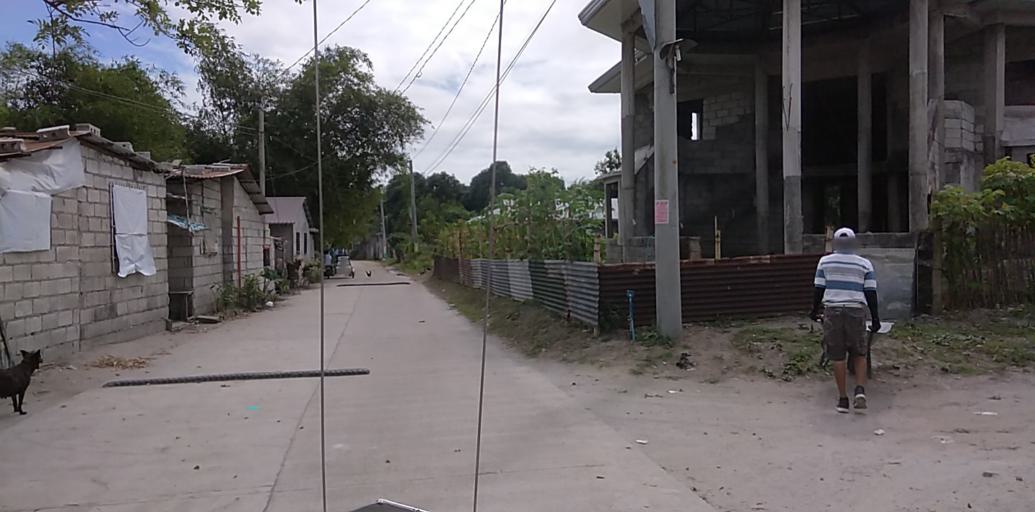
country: PH
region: Central Luzon
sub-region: Province of Pampanga
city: Porac
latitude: 15.0639
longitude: 120.5403
